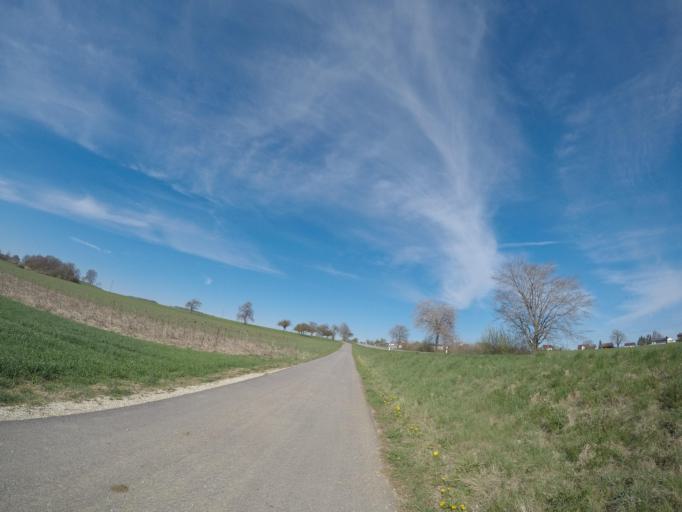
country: DE
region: Baden-Wuerttemberg
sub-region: Tuebingen Region
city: Mehrstetten
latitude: 48.3478
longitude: 9.6161
